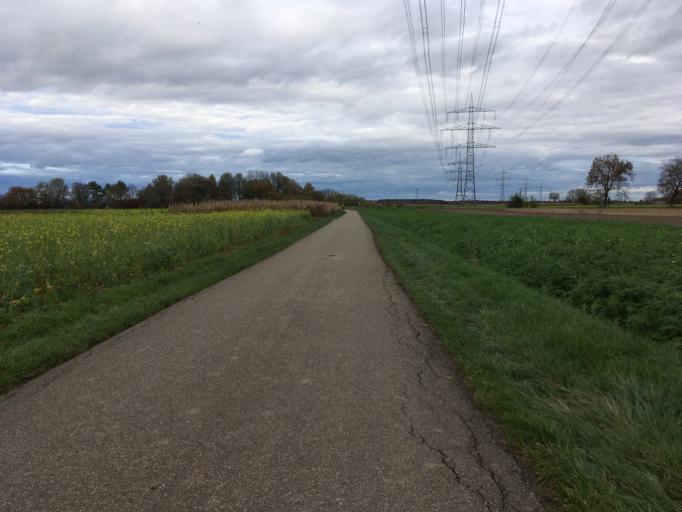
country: DE
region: Baden-Wuerttemberg
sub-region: Freiburg Region
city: Riegel
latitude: 48.1484
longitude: 7.7365
